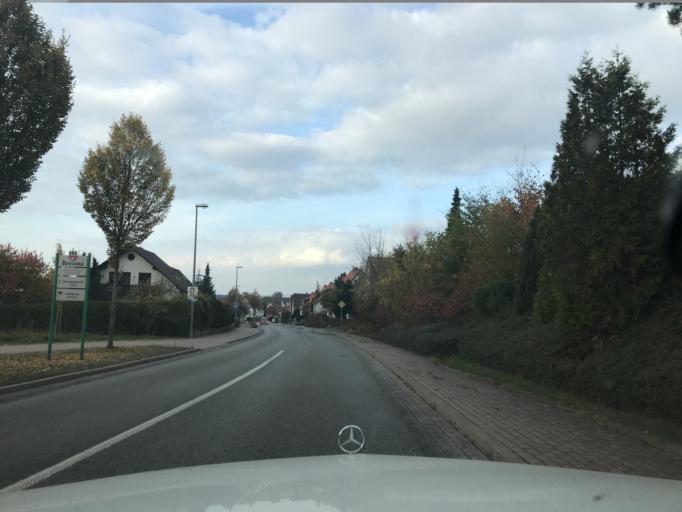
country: DE
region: Hesse
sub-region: Regierungsbezirk Kassel
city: Breuna
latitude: 51.4097
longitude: 9.1830
